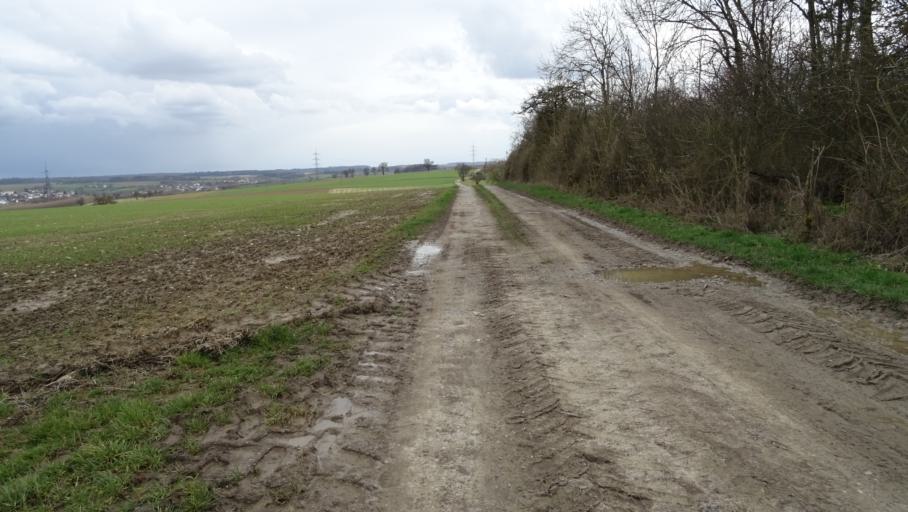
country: DE
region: Baden-Wuerttemberg
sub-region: Karlsruhe Region
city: Limbach
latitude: 49.4278
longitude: 9.2605
